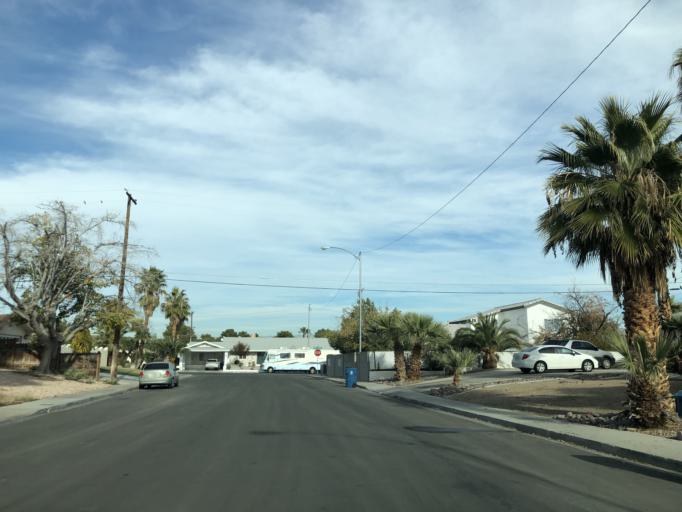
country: US
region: Nevada
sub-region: Clark County
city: Winchester
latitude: 36.1193
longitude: -115.1200
